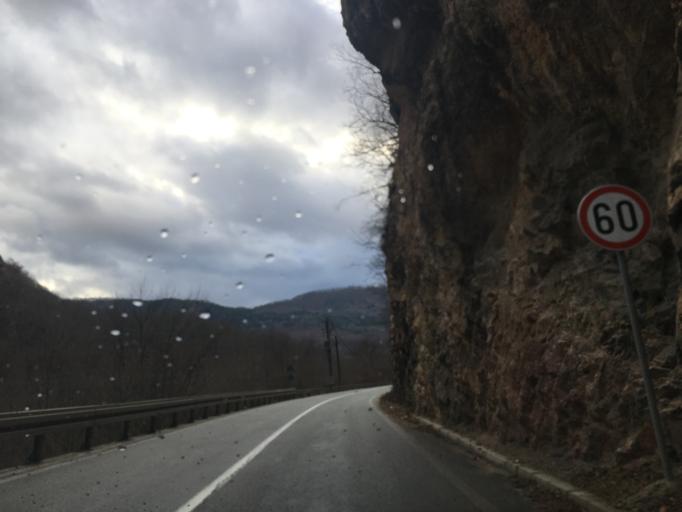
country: RS
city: Sokolovo Brdo
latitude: 43.1911
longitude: 19.7685
